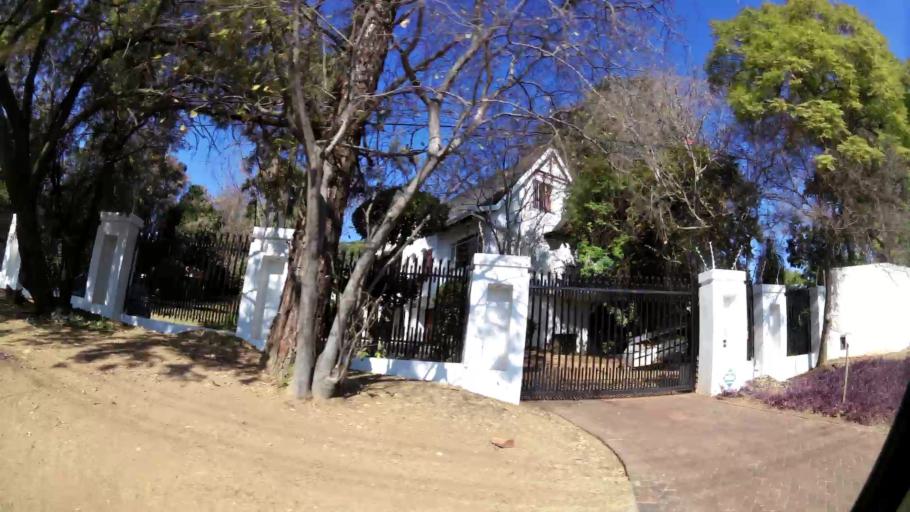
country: ZA
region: Gauteng
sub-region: City of Tshwane Metropolitan Municipality
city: Pretoria
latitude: -25.7901
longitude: 28.2551
